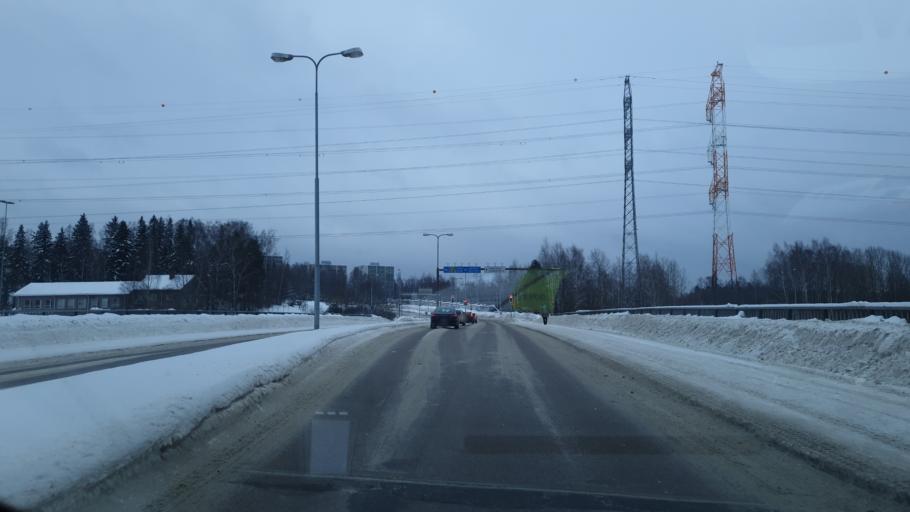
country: FI
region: Uusimaa
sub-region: Helsinki
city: Vantaa
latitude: 60.2685
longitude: 25.1014
